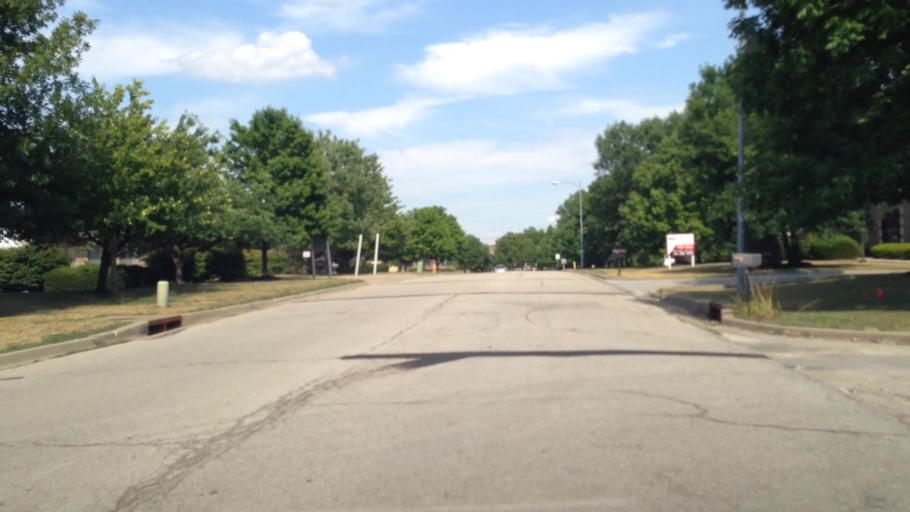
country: US
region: Kansas
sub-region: Johnson County
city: Lenexa
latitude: 38.9184
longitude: -94.7589
